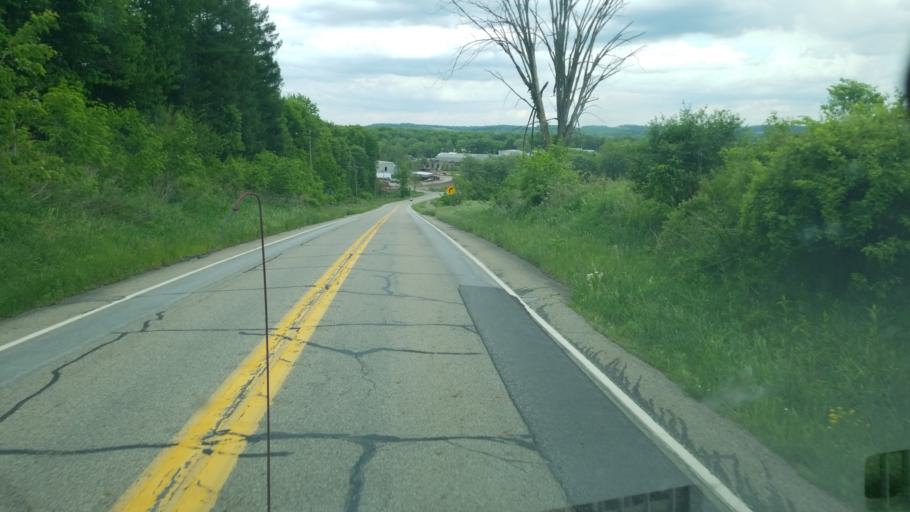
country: US
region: Pennsylvania
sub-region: Venango County
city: Franklin
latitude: 41.2012
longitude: -79.8024
